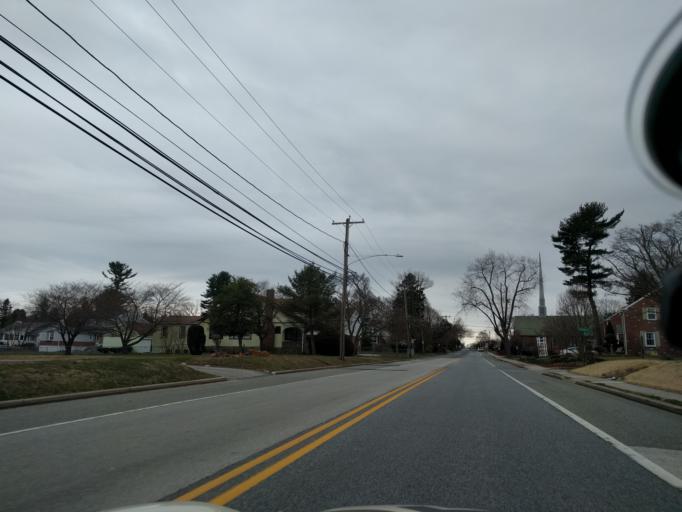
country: US
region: Pennsylvania
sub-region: Delaware County
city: Broomall
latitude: 39.9813
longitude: -75.3819
